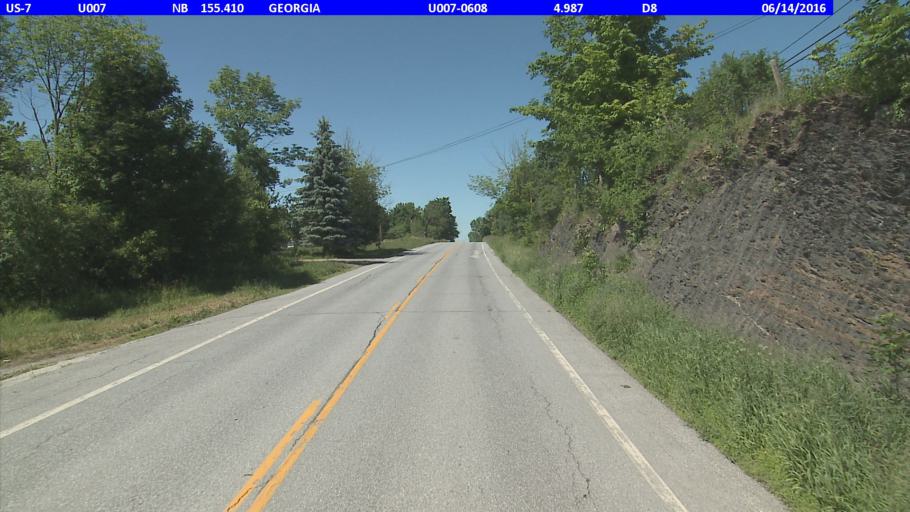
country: US
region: Vermont
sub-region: Franklin County
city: Saint Albans
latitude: 44.7431
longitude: -73.1142
